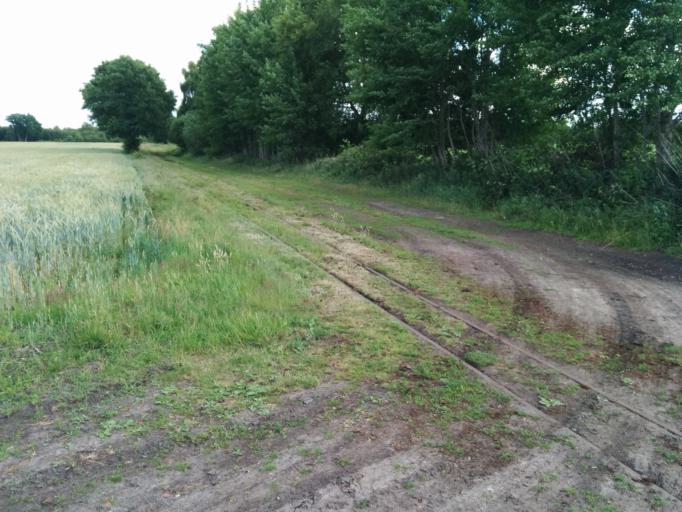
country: DE
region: Lower Saxony
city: Lohne
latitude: 52.6614
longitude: 8.2848
